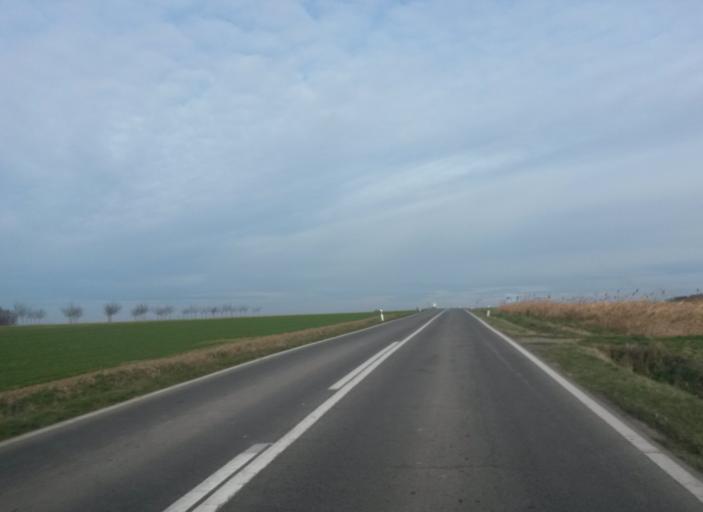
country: HR
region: Osjecko-Baranjska
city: Viskovci
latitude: 45.3732
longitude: 18.4374
